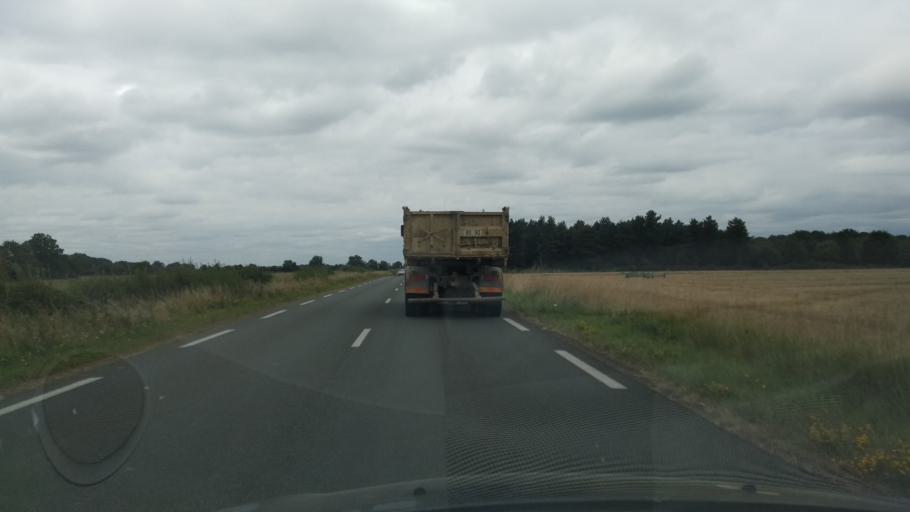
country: FR
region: Poitou-Charentes
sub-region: Departement de la Vienne
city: Saint-Maurice-la-Clouere
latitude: 46.4017
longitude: 0.3939
